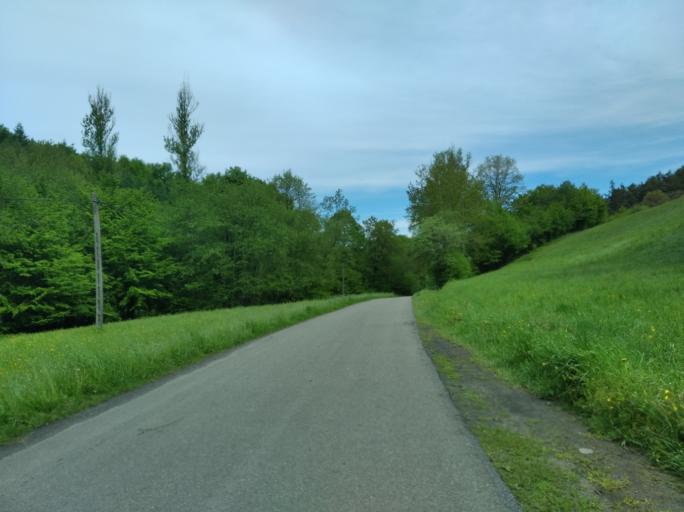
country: PL
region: Subcarpathian Voivodeship
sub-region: Powiat strzyzowski
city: Strzyzow
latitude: 49.9216
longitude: 21.7543
